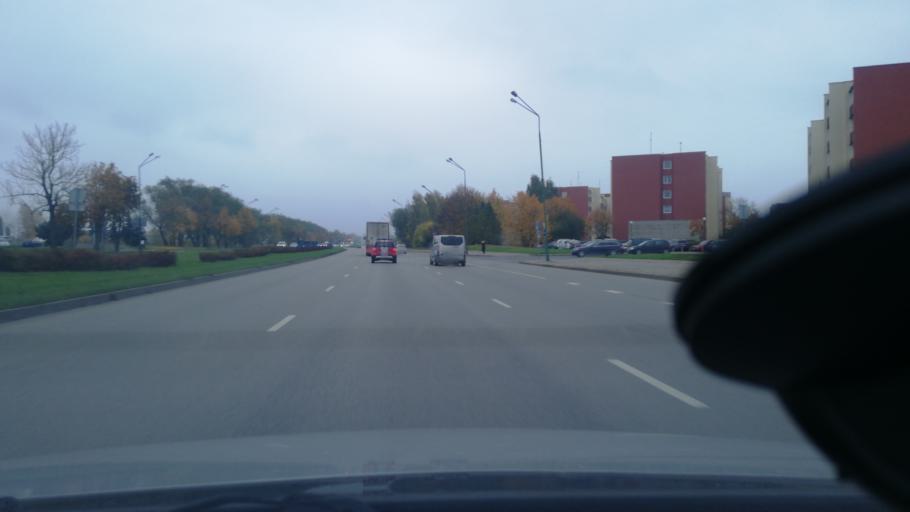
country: LT
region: Klaipedos apskritis
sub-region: Klaipeda
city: Klaipeda
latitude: 55.6770
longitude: 21.1897
